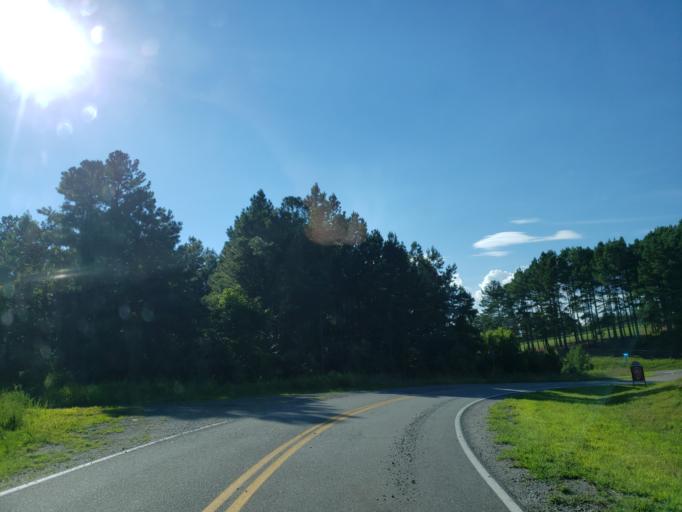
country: US
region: Georgia
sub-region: Bartow County
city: Rydal
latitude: 34.3574
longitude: -84.6106
